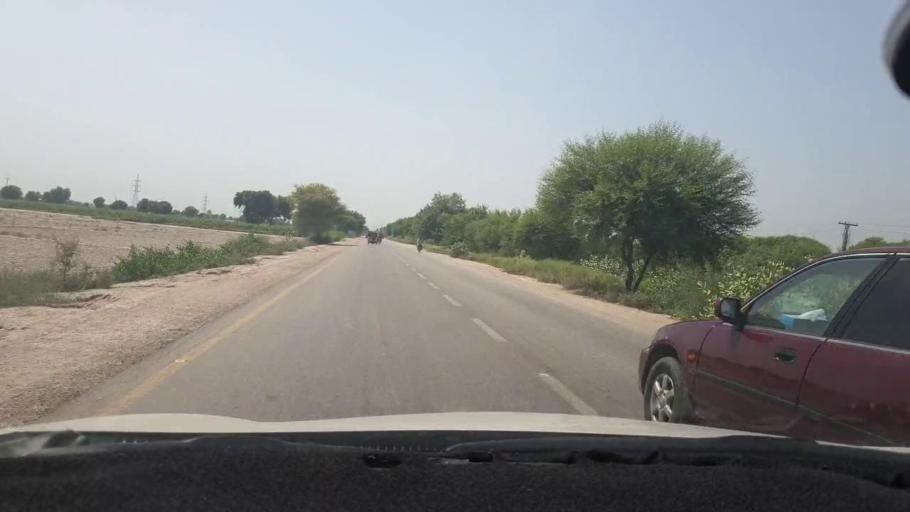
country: PK
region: Sindh
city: Bhit Shah
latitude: 25.8482
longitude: 68.4819
